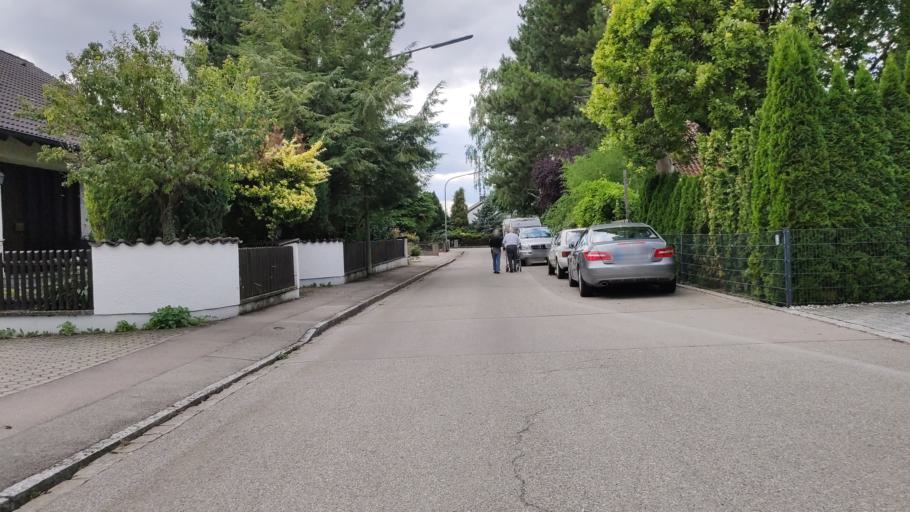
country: DE
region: Bavaria
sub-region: Swabia
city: Konigsbrunn
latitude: 48.2529
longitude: 10.8959
